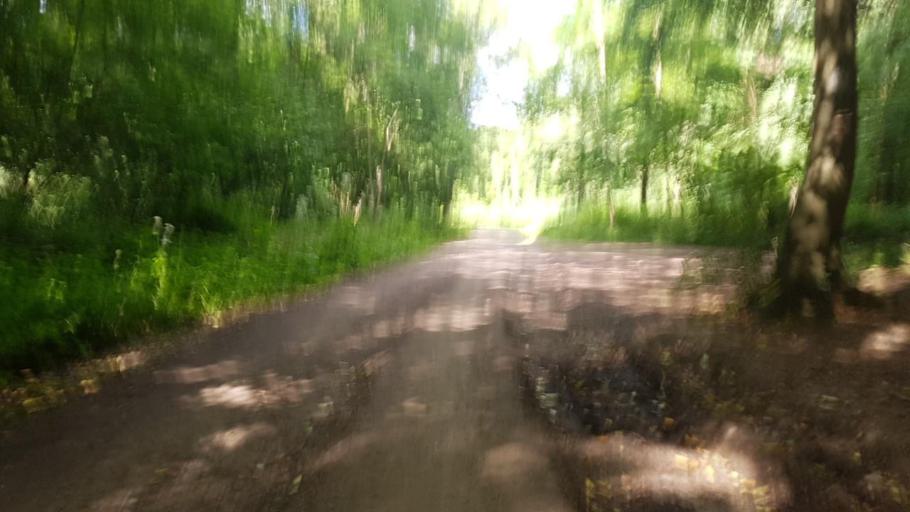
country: BE
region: Wallonia
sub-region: Province du Hainaut
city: Charleroi
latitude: 50.3631
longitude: 4.4519
